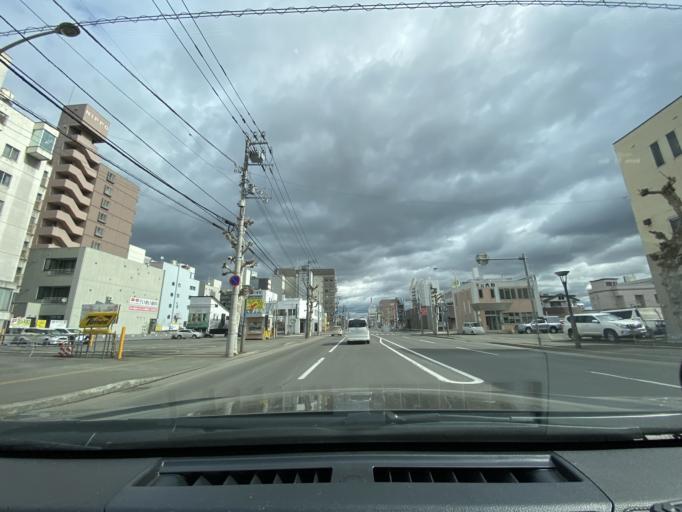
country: JP
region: Hokkaido
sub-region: Asahikawa-shi
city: Asahikawa
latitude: 43.7663
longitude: 142.3631
